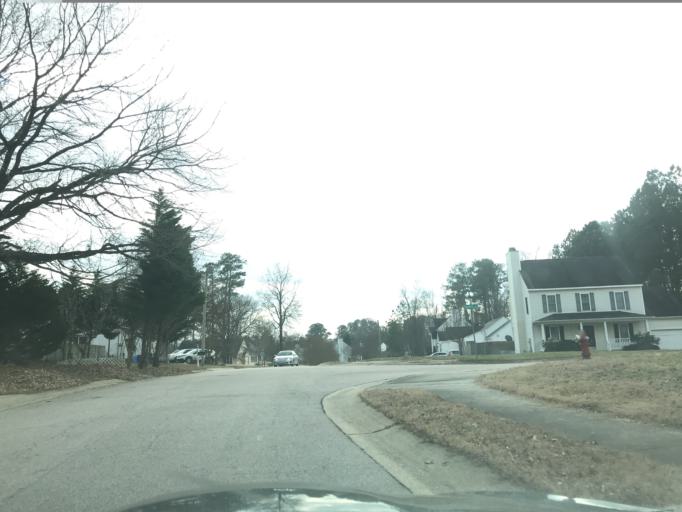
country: US
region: North Carolina
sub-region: Wake County
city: Raleigh
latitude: 35.8210
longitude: -78.5787
